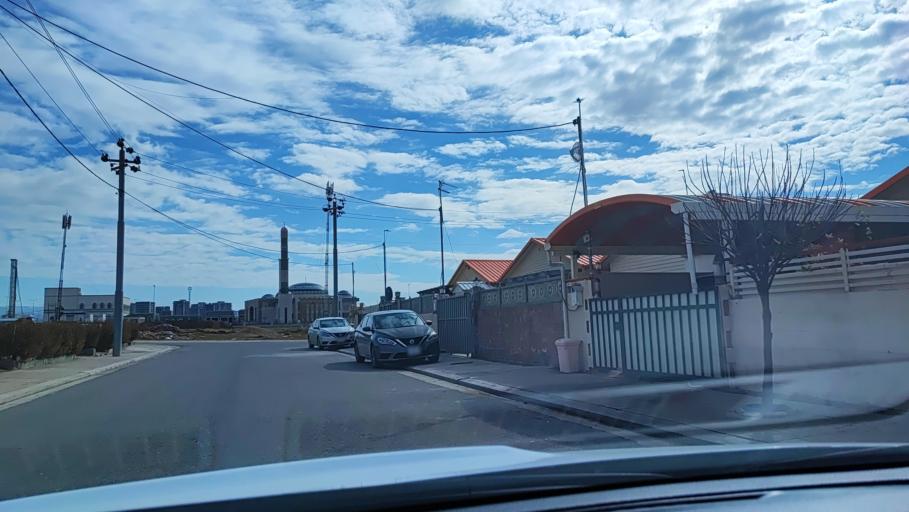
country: IQ
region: Arbil
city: Erbil
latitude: 36.2853
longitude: 44.0698
